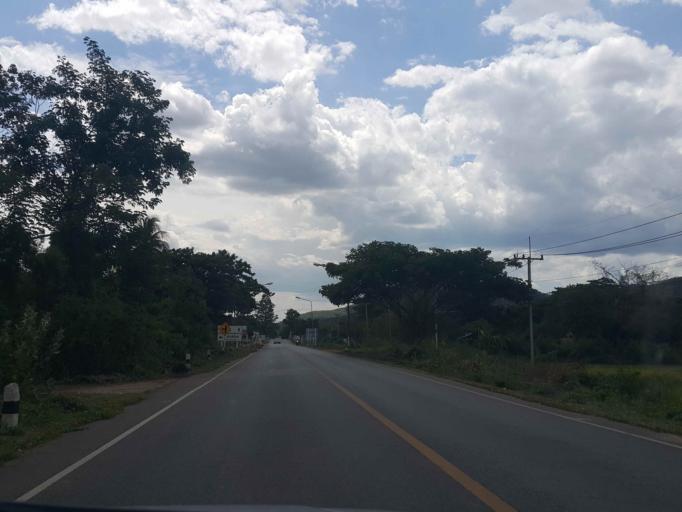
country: TH
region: Sukhothai
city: Thung Saliam
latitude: 17.3279
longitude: 99.5059
